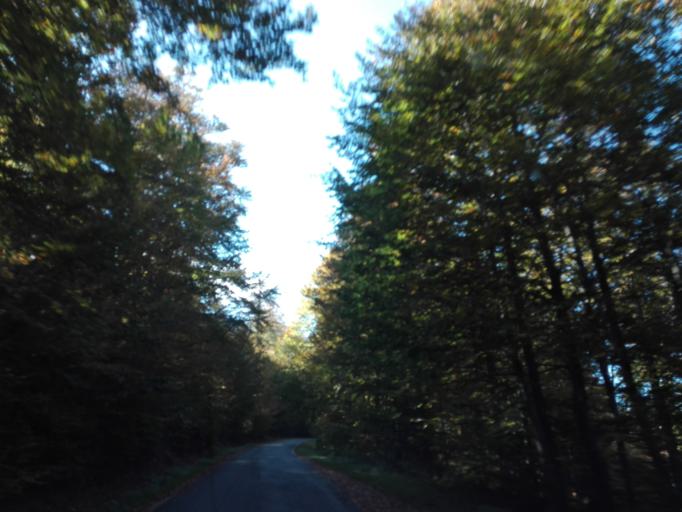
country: ES
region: Navarre
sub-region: Provincia de Navarra
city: Oronz
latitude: 42.9692
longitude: -1.1280
